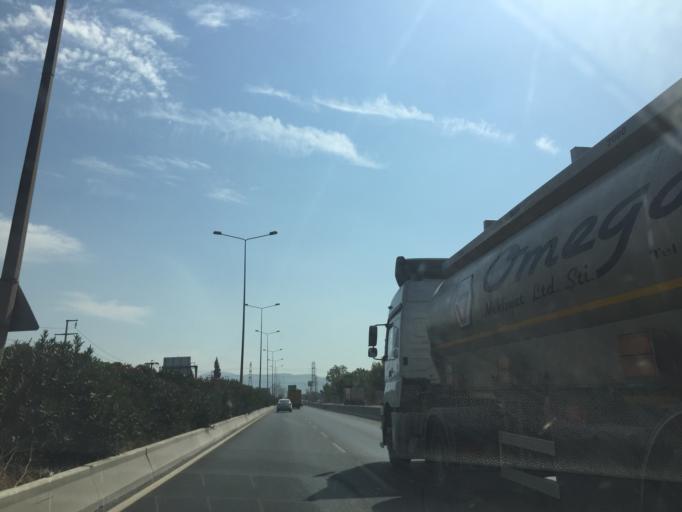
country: TR
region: Izmir
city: Bornova
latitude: 38.4605
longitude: 27.2348
